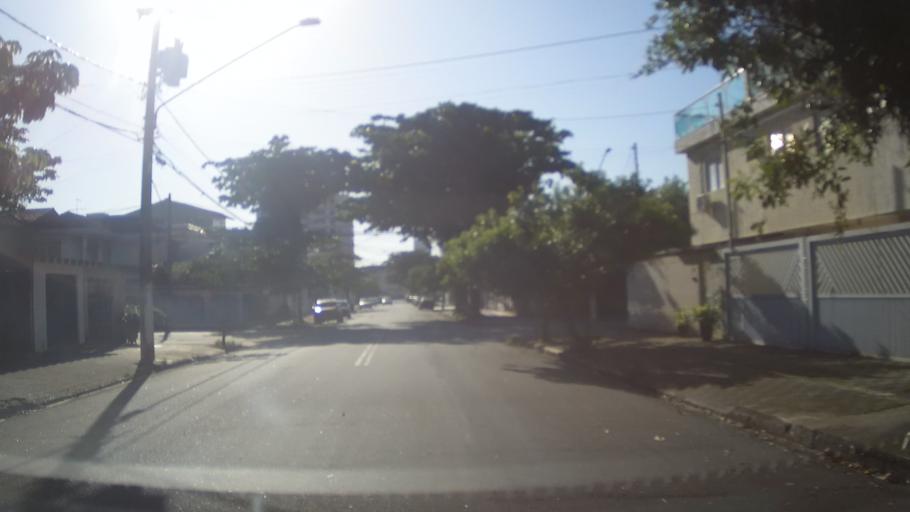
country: BR
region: Sao Paulo
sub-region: Santos
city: Santos
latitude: -23.9487
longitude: -46.3429
